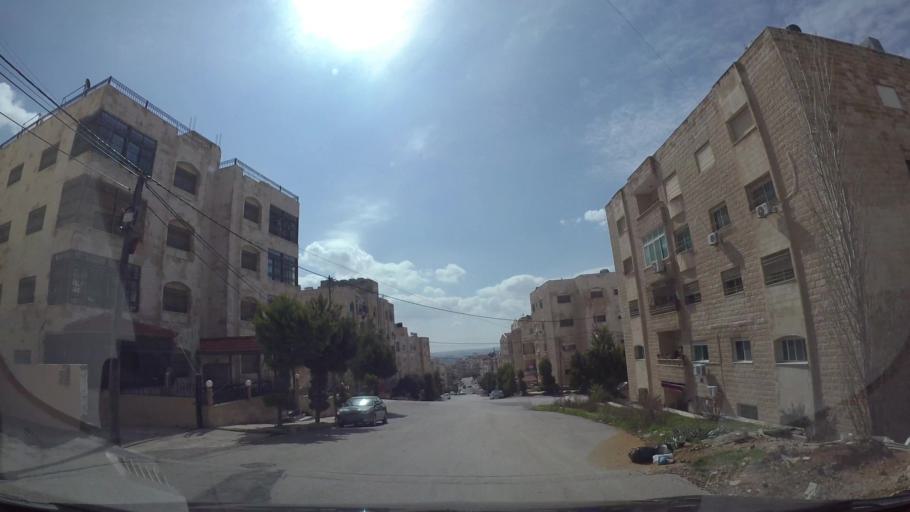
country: JO
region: Amman
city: Al Jubayhah
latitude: 31.9974
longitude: 35.9069
